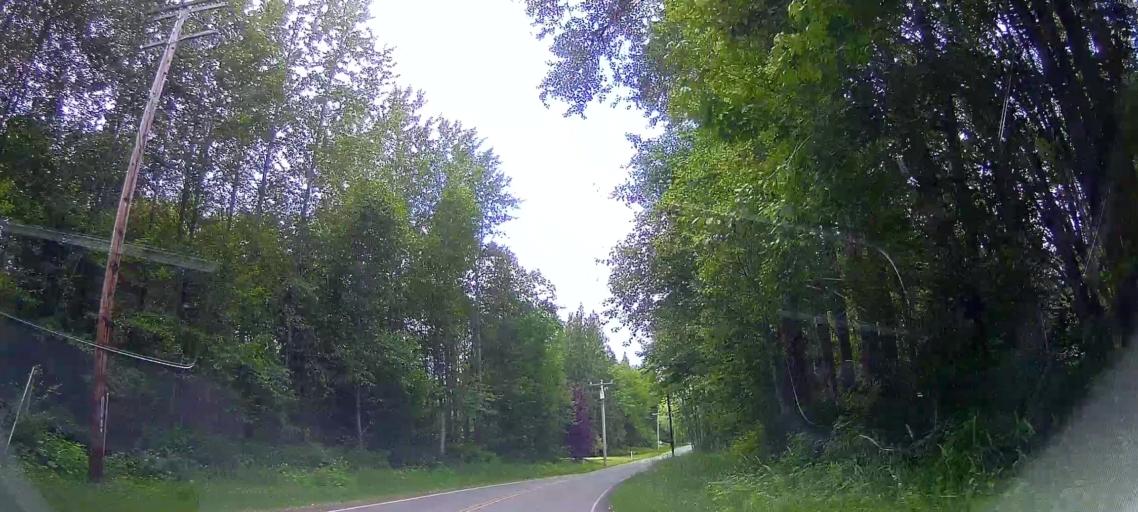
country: US
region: Washington
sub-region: Whatcom County
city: Sudden Valley
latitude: 48.6779
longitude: -122.1679
